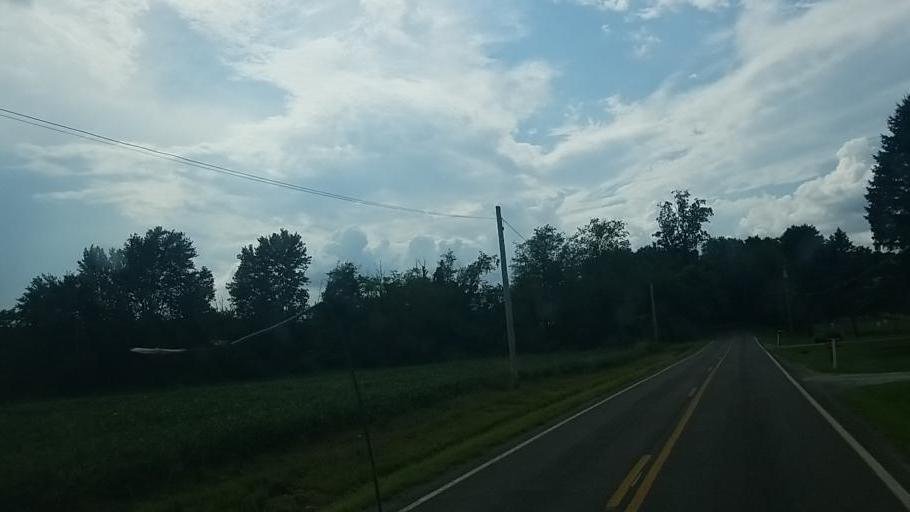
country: US
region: Ohio
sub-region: Wayne County
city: Creston
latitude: 41.0032
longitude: -81.9018
